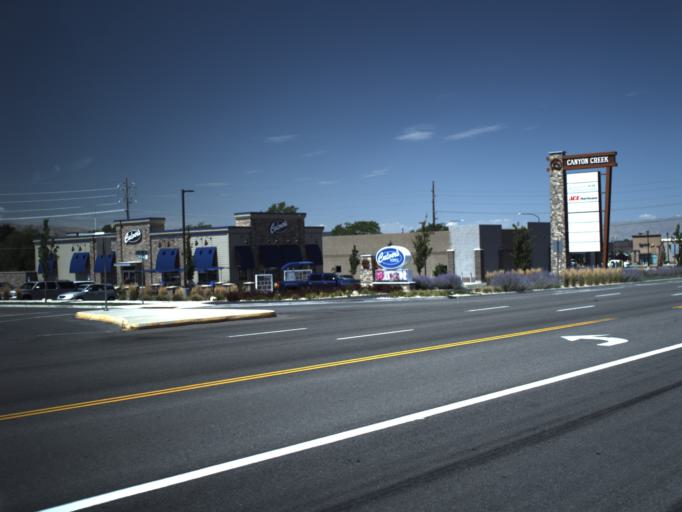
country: US
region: Utah
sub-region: Utah County
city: Spanish Fork
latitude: 40.1220
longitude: -111.6420
